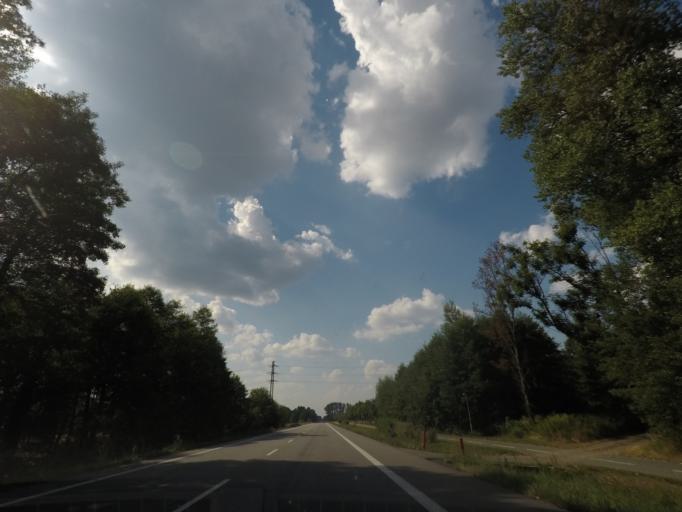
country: CZ
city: Albrechtice nad Orlici
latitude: 50.1617
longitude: 16.0564
